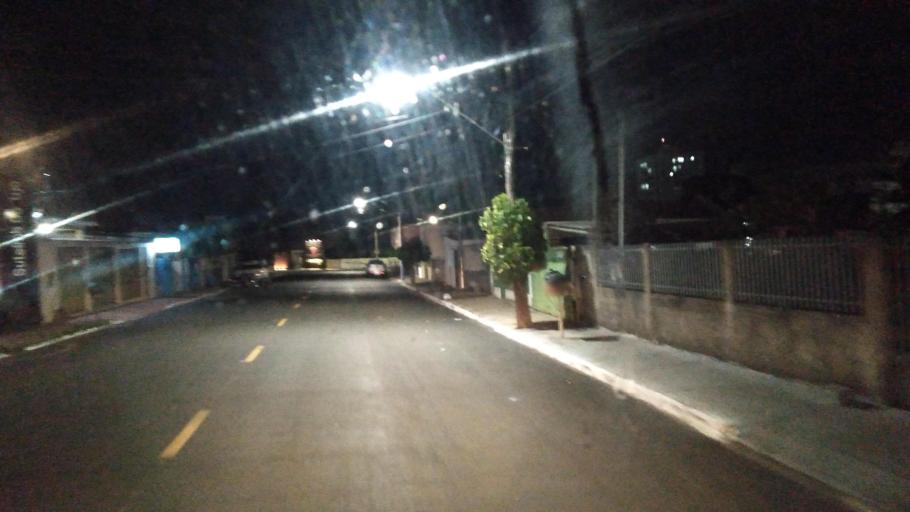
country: BR
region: Goias
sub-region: Mineiros
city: Mineiros
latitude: -17.5659
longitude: -52.5591
